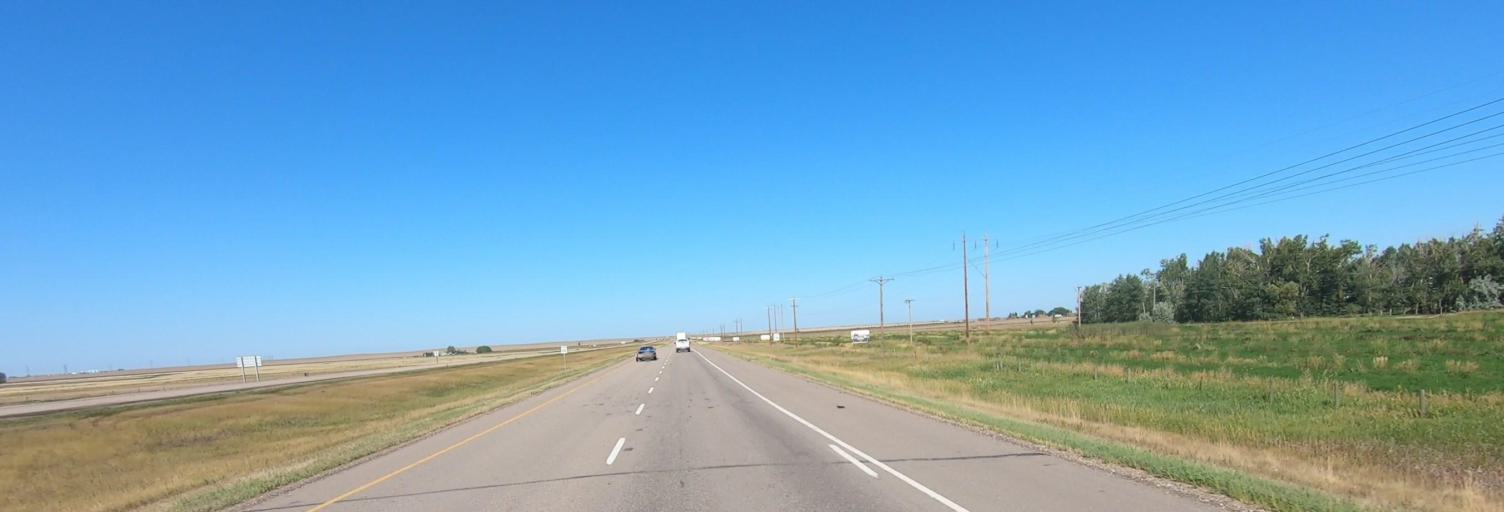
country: CA
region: Alberta
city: Brooks
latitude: 50.4891
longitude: -111.6569
